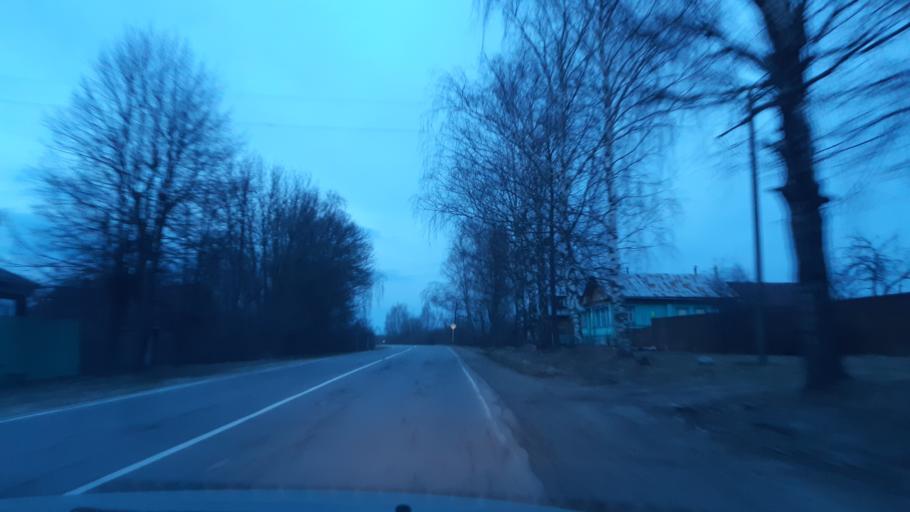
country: RU
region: Vladimir
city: Luknovo
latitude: 56.1888
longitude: 42.0226
